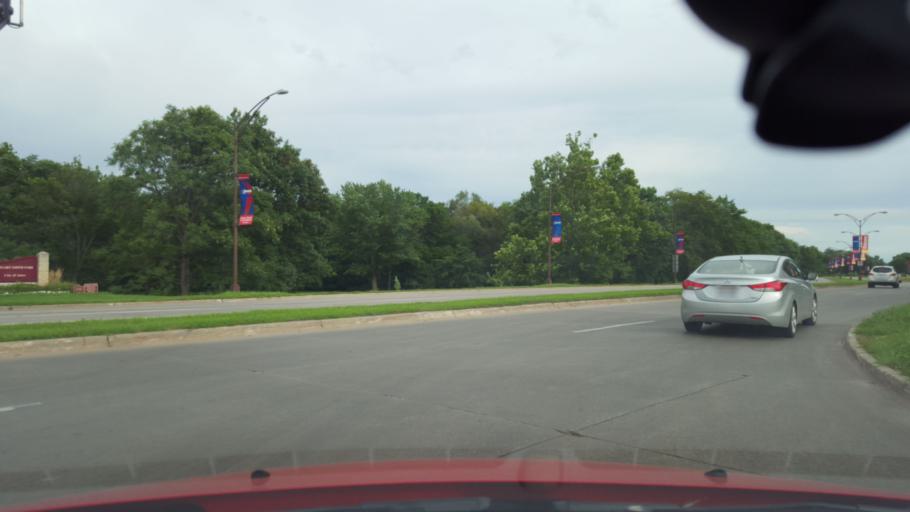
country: US
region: Iowa
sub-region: Story County
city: Ames
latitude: 42.0227
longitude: -93.6336
